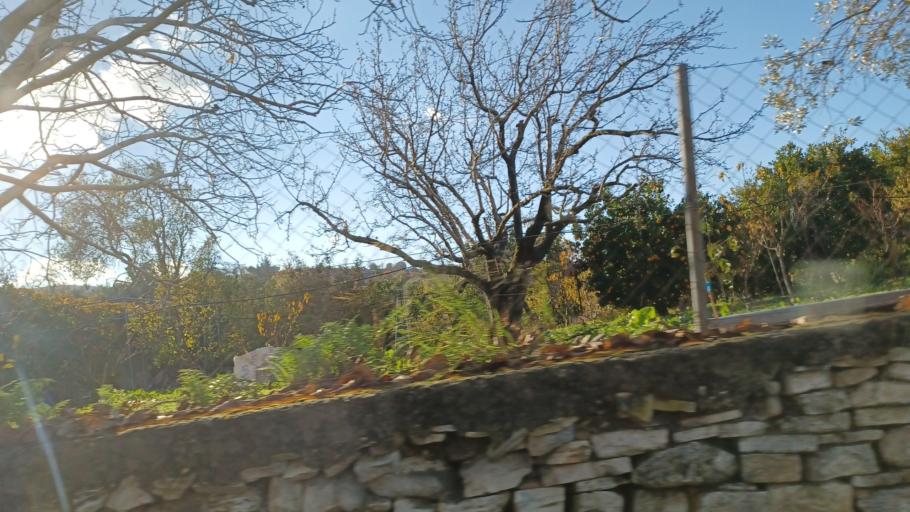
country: CY
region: Limassol
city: Pachna
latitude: 34.8527
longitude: 32.7412
